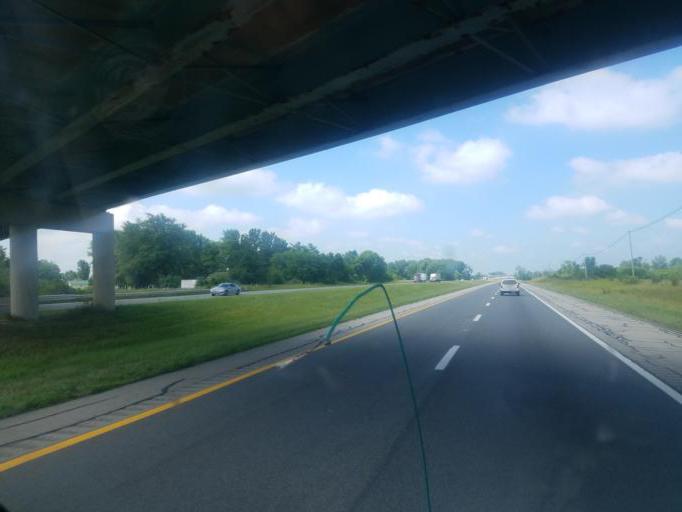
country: US
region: Ohio
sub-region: Fayette County
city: Jeffersonville
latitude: 39.6704
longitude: -83.5041
